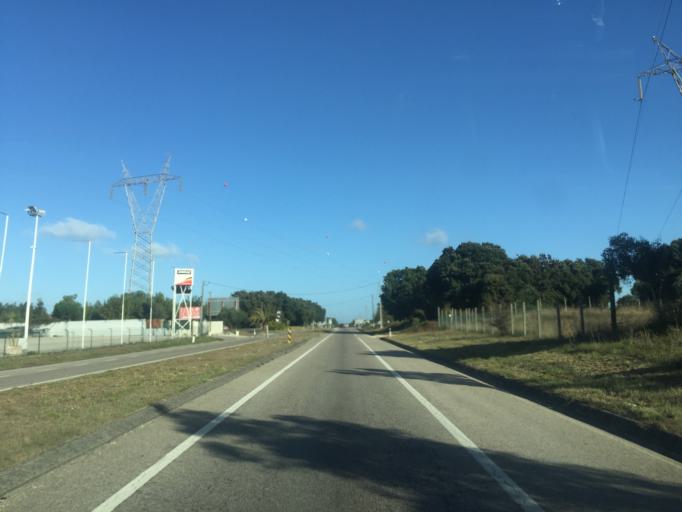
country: PT
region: Leiria
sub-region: Alcobaca
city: Benedita
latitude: 39.4065
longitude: -8.9617
